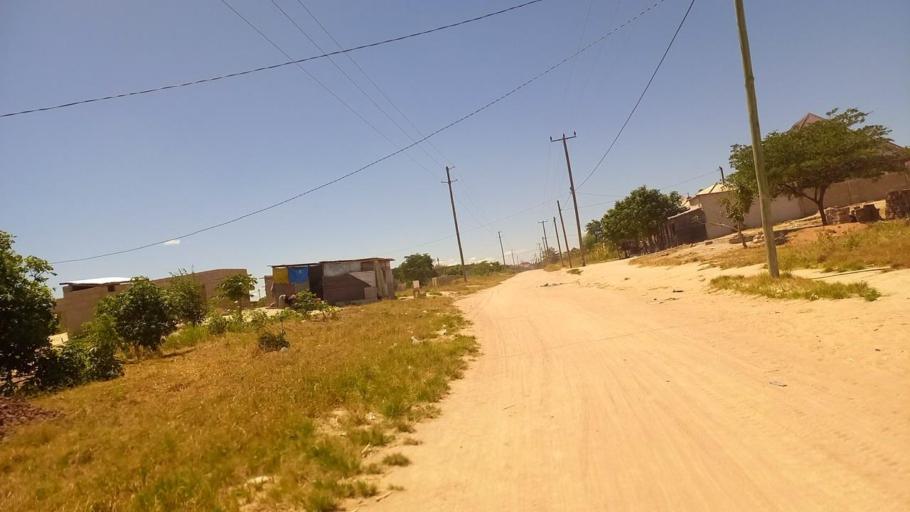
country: TZ
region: Dodoma
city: Dodoma
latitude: -6.1314
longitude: 35.7234
